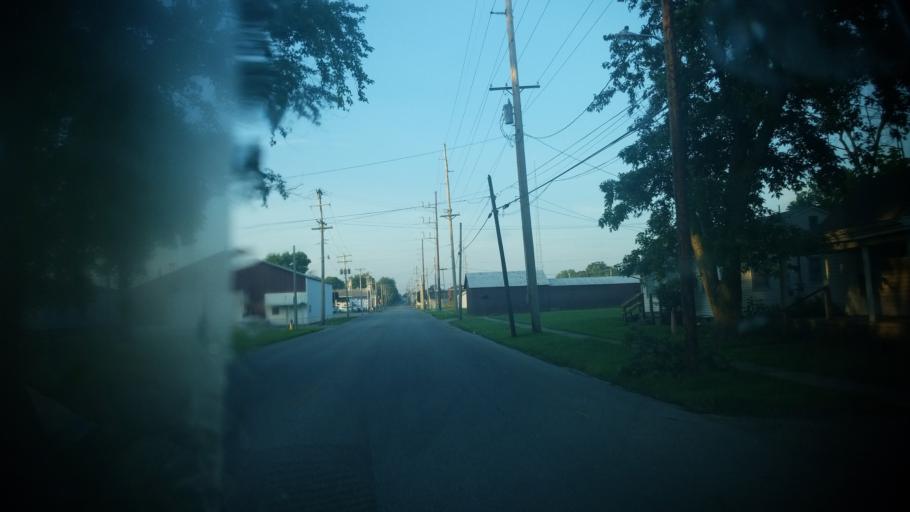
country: US
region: Illinois
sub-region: Wayne County
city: Fairfield
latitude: 38.3820
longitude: -88.3684
